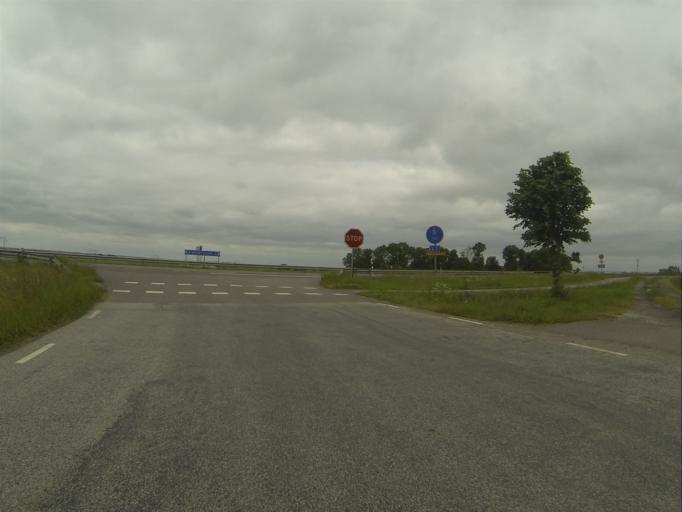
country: SE
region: Skane
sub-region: Staffanstorps Kommun
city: Staffanstorp
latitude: 55.6820
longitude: 13.2767
